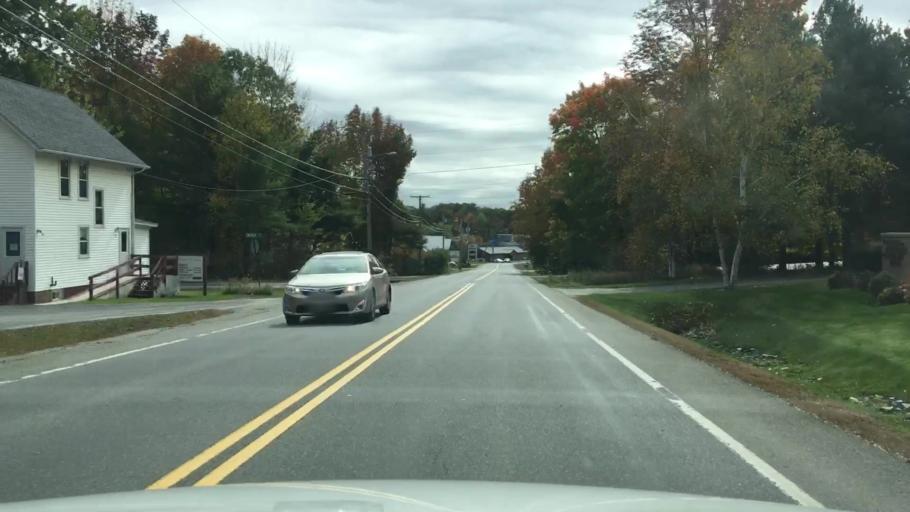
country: US
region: Maine
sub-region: Kennebec County
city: Waterville
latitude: 44.5483
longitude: -69.6765
